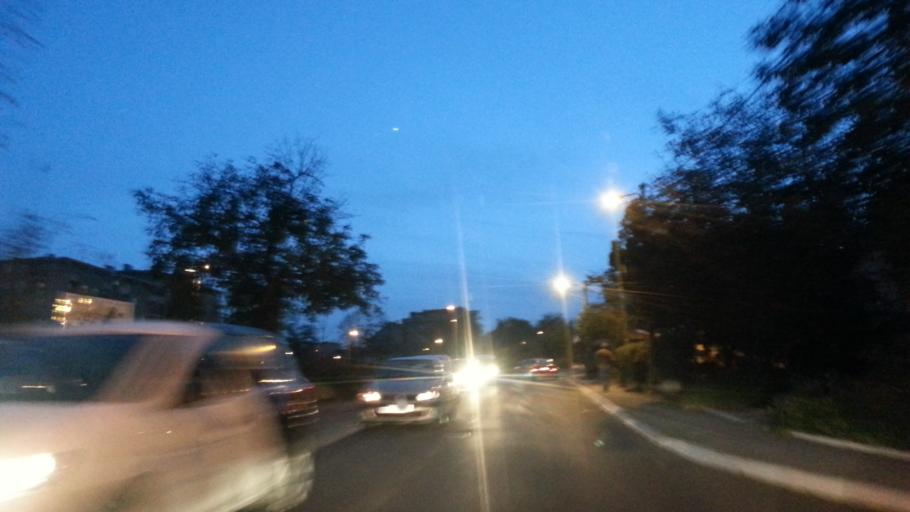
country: RS
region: Central Serbia
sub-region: Belgrade
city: Vozdovac
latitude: 44.7620
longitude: 20.4876
